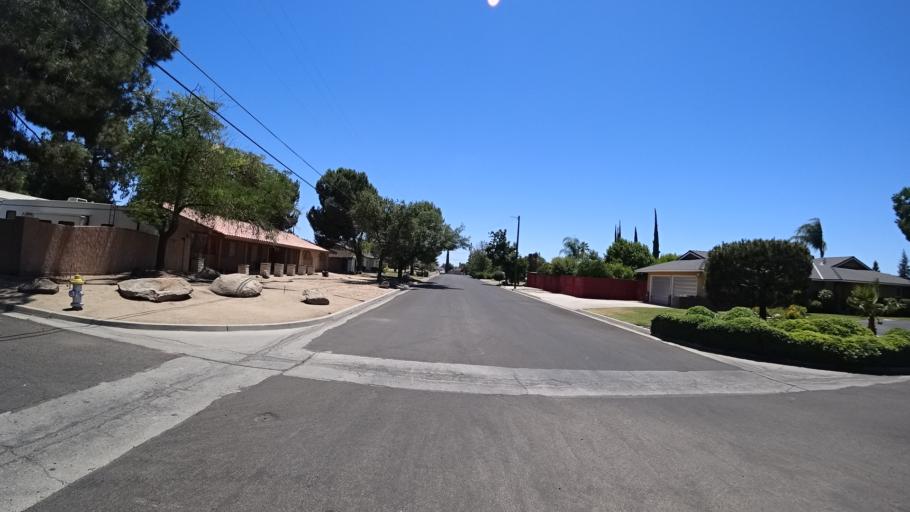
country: US
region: California
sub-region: Fresno County
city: Tarpey Village
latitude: 36.8031
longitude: -119.7520
